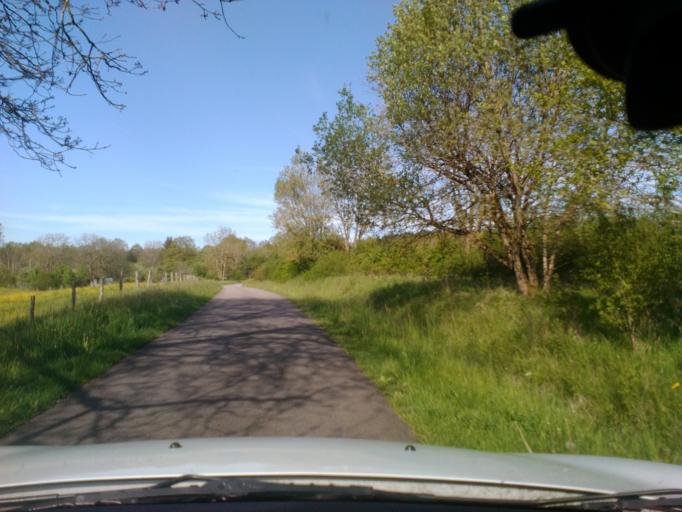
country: FR
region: Lorraine
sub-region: Departement des Vosges
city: Mirecourt
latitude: 48.2752
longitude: 6.1274
